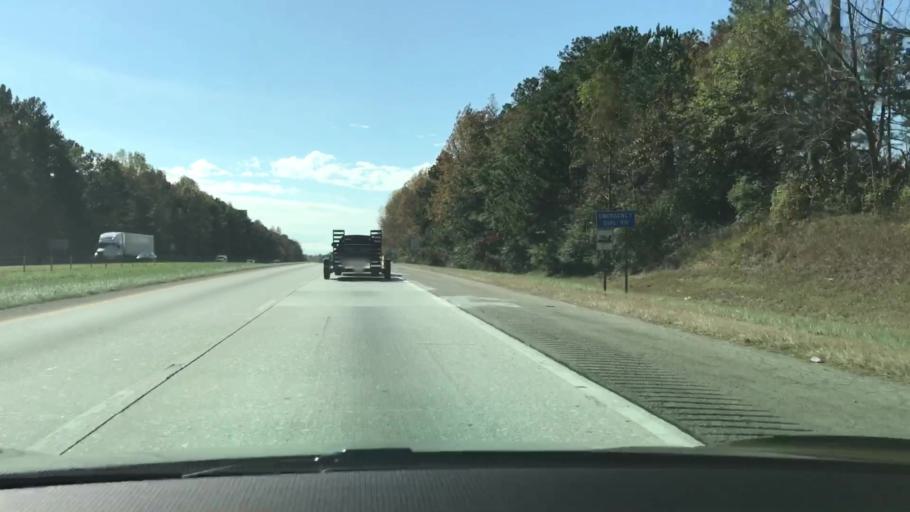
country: US
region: Georgia
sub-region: Gwinnett County
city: Buford
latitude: 34.1313
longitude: -83.9599
